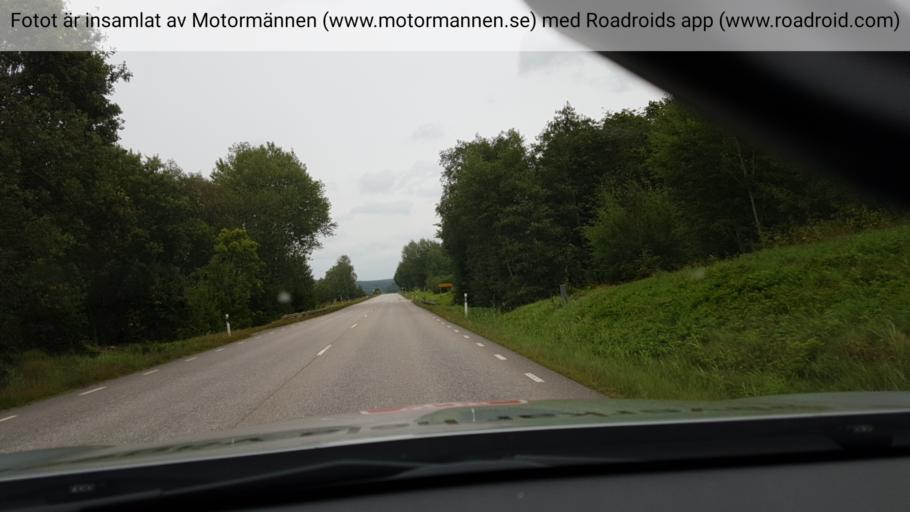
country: SE
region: Vaestra Goetaland
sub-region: Molndal
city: Lindome
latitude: 57.5889
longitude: 12.1289
